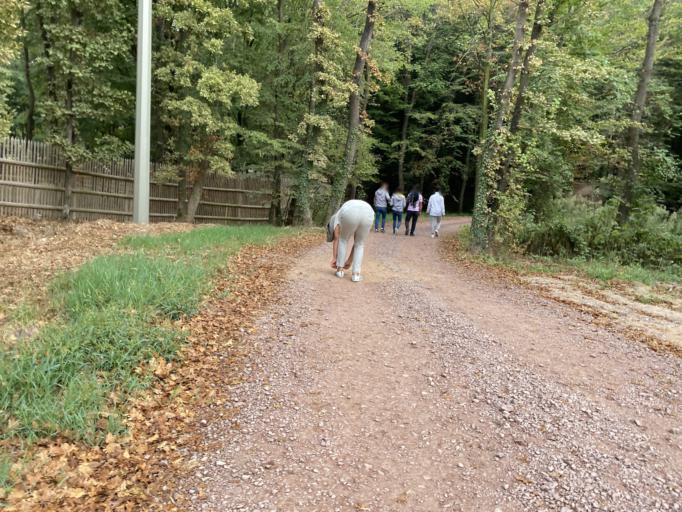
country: TR
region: Kocaeli
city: Derbent
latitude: 40.7356
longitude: 30.1600
